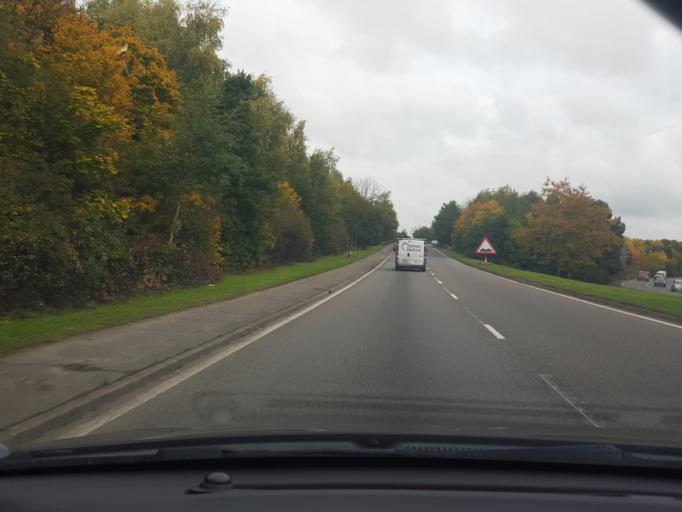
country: GB
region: England
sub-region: Essex
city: Colchester
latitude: 51.9229
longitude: 0.9351
